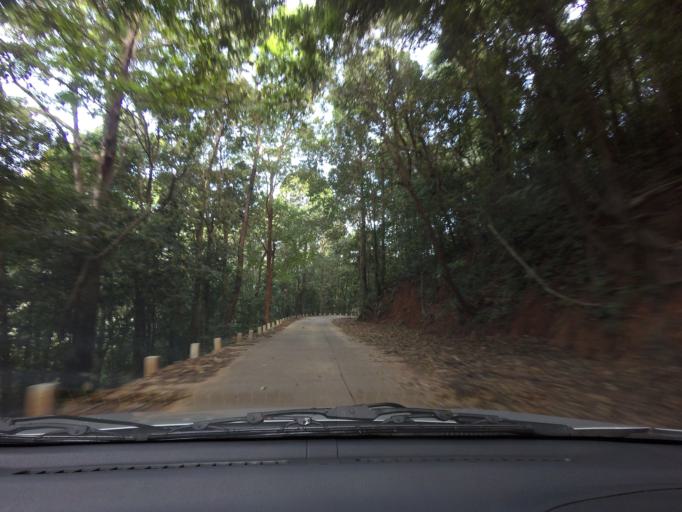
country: IN
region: Karnataka
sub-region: Kodagu
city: Somvarpet
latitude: 12.7229
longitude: 75.6620
